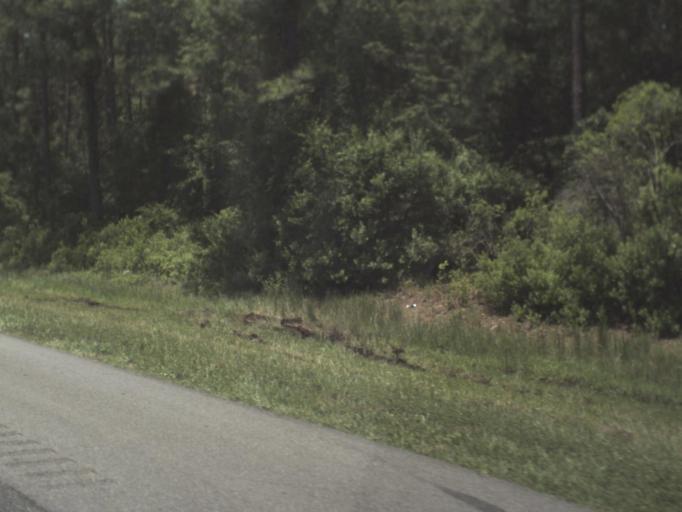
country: US
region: Florida
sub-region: Columbia County
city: Five Points
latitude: 30.2428
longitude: -82.6496
